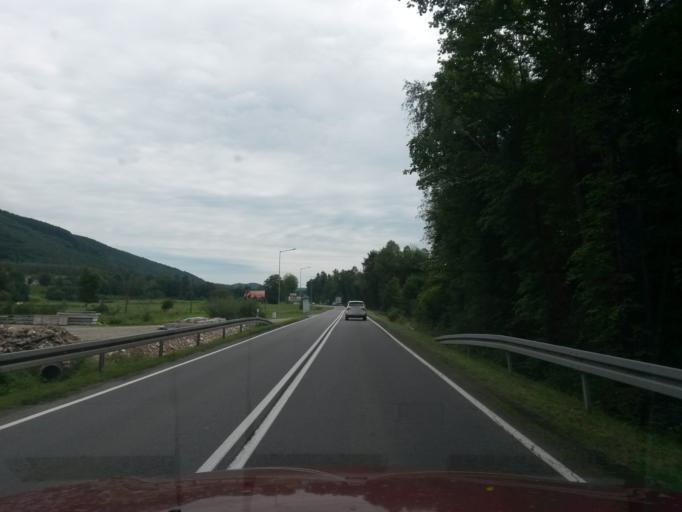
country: PL
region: Lesser Poland Voivodeship
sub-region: Powiat nowosadecki
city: Kamionka Wielka
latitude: 49.5414
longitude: 20.7947
